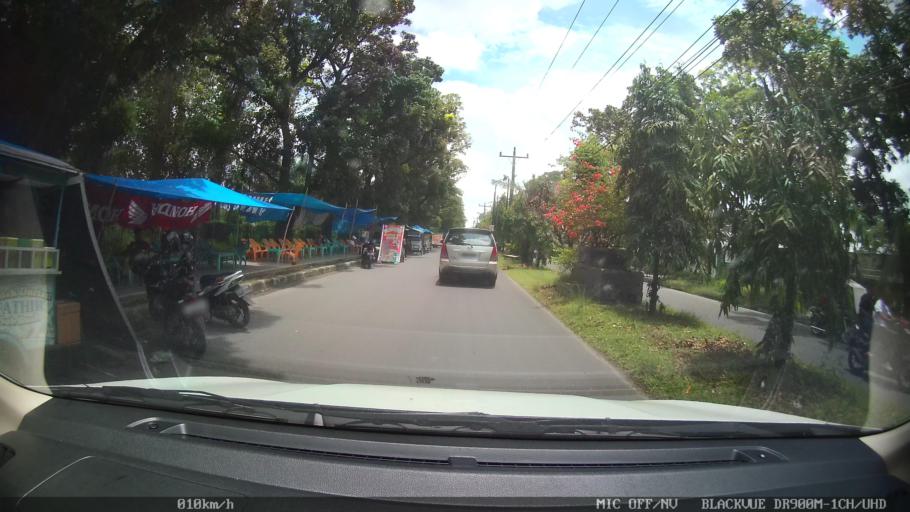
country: ID
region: North Sumatra
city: Medan
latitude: 3.6144
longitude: 98.7076
